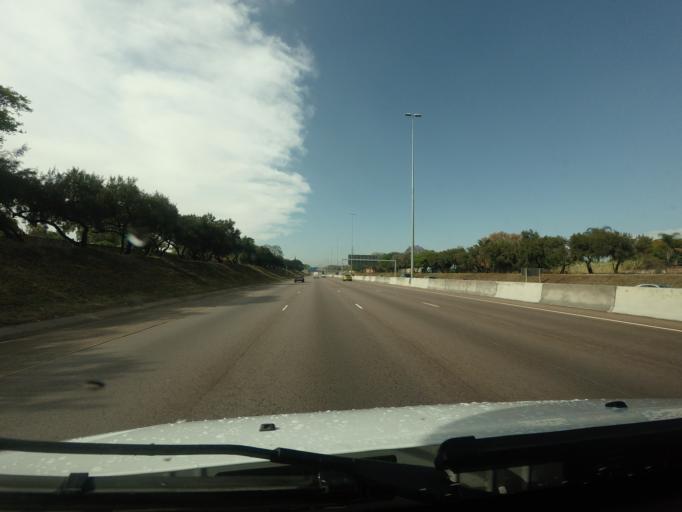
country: ZA
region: Gauteng
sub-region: City of Tshwane Metropolitan Municipality
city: Pretoria
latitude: -25.7216
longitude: 28.2654
